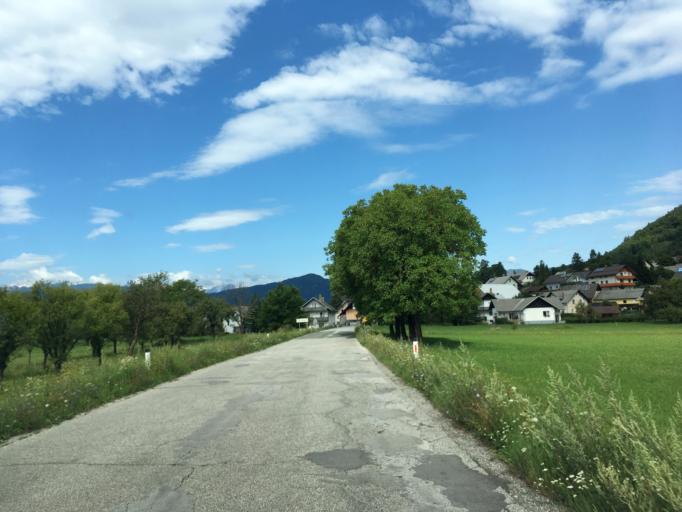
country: SI
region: Zirovnica
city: Zirovnica
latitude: 46.3944
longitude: 14.1571
